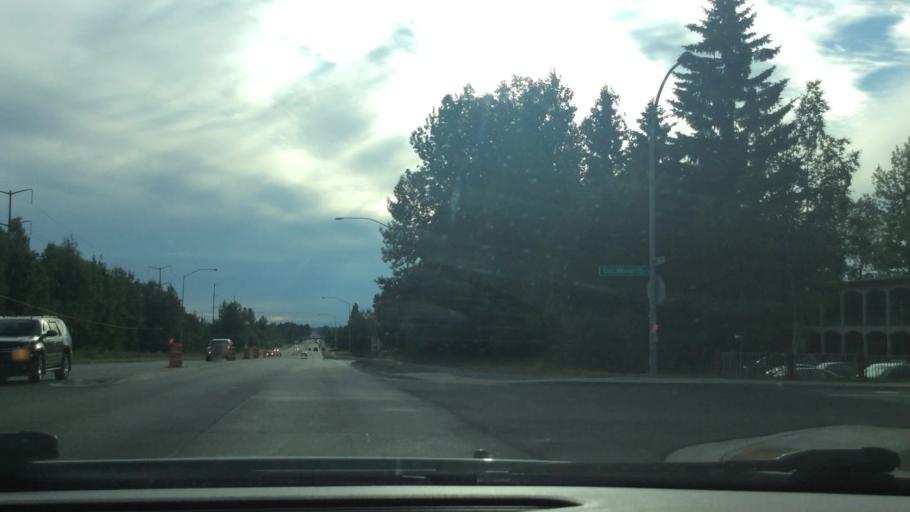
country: US
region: Alaska
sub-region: Anchorage Municipality
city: Anchorage
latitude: 61.1808
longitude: -149.7854
